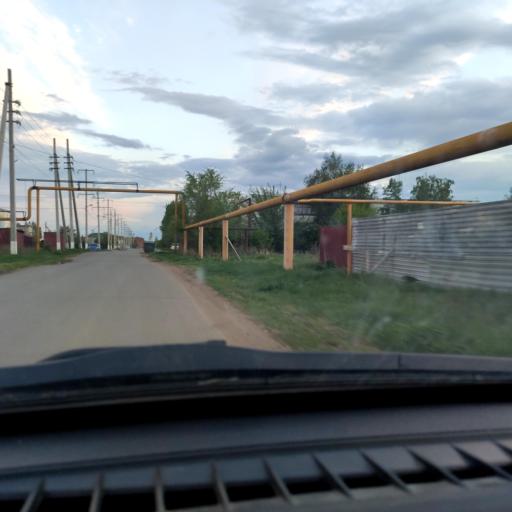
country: RU
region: Samara
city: Podstepki
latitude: 53.5201
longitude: 49.1129
